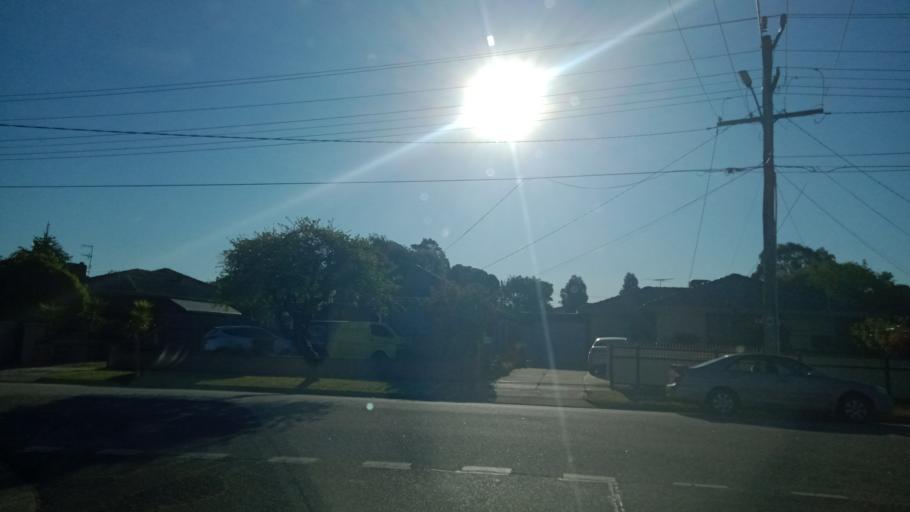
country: AU
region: Victoria
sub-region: Greater Dandenong
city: Springvale
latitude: -37.9333
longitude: 145.1721
